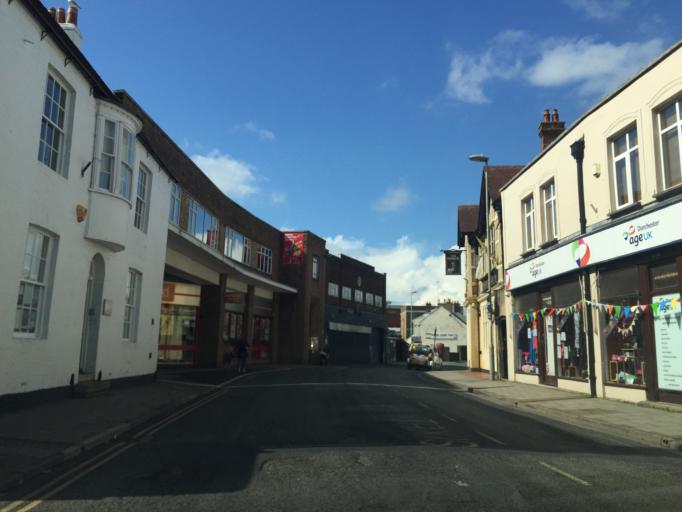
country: GB
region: England
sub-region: Dorset
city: Dorchester
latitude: 50.7120
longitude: -2.4380
